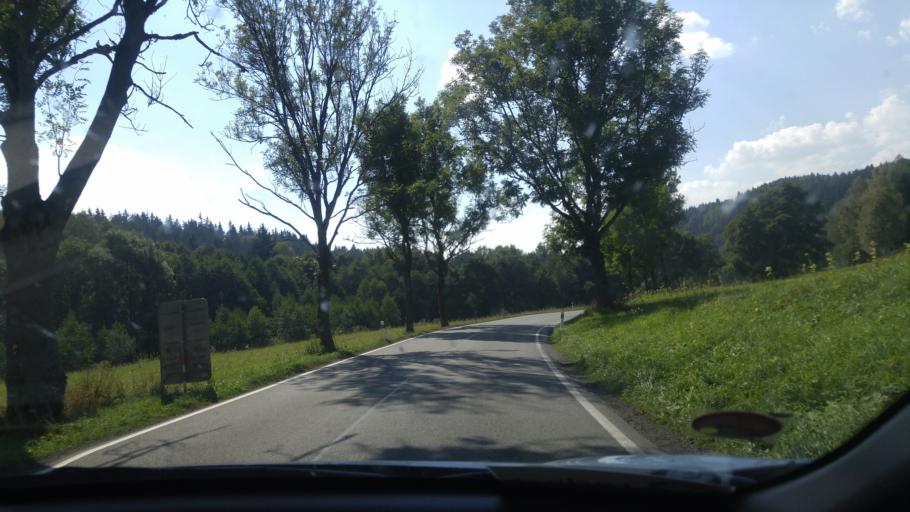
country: CZ
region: Olomoucky
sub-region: Okres Sumperk
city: Stare Mesto
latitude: 50.1731
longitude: 17.0377
